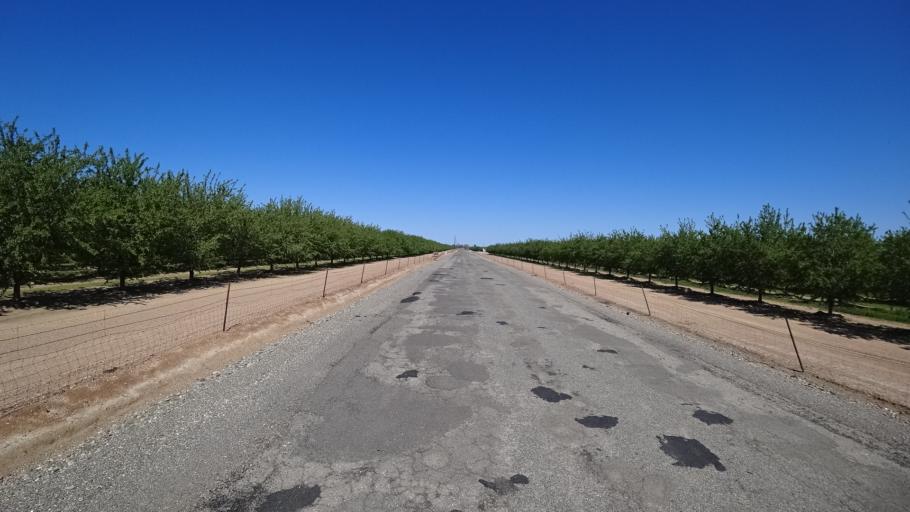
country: US
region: California
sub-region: Glenn County
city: Orland
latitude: 39.6553
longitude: -122.2346
